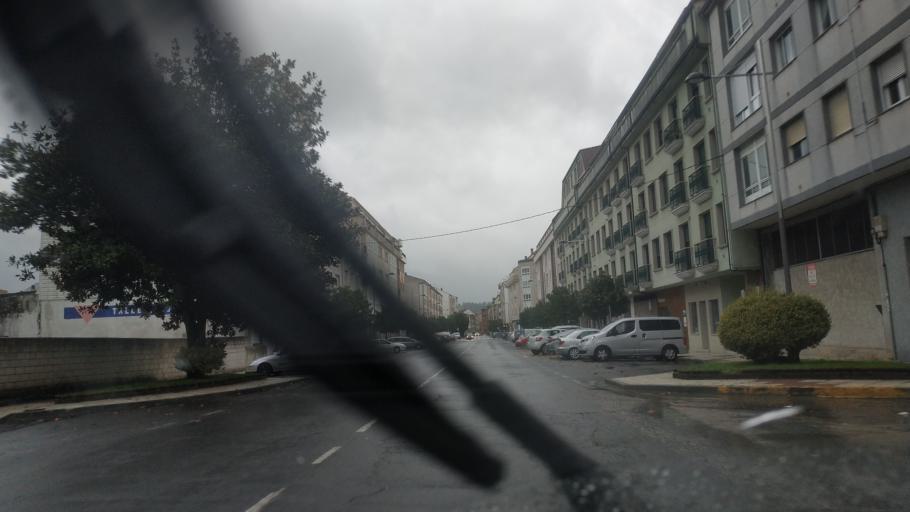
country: ES
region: Galicia
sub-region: Provincia da Coruna
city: Negreira
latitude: 42.9144
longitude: -8.7357
